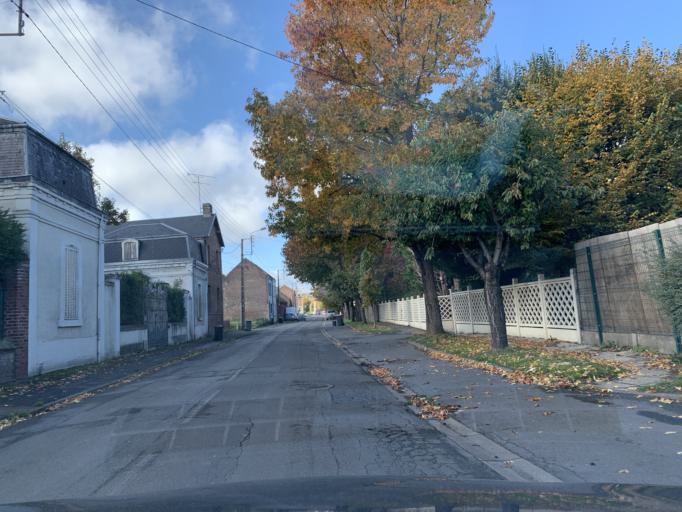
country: FR
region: Nord-Pas-de-Calais
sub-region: Departement du Nord
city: Neuville-Saint-Remy
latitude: 50.1856
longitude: 3.2462
